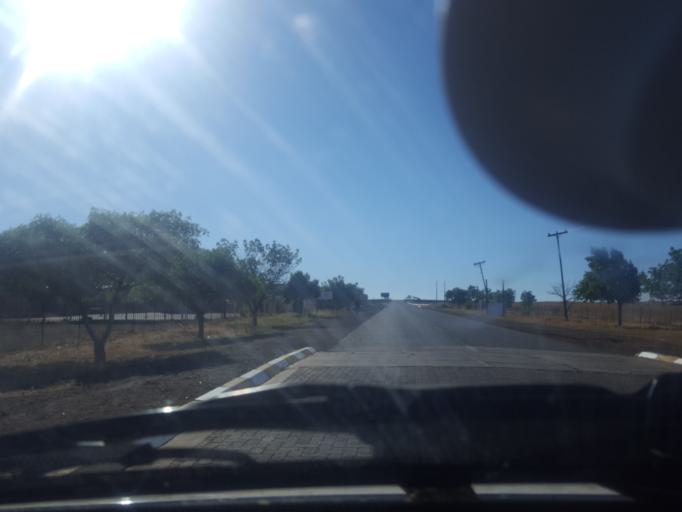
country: ZA
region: Orange Free State
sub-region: Xhariep District Municipality
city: Trompsburg
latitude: -30.0341
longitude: 25.7874
